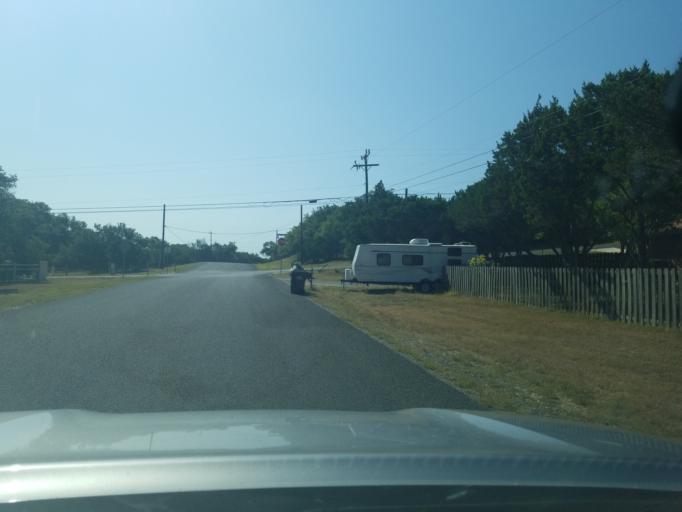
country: US
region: Texas
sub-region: Bexar County
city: Timberwood Park
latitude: 29.6747
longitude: -98.5096
